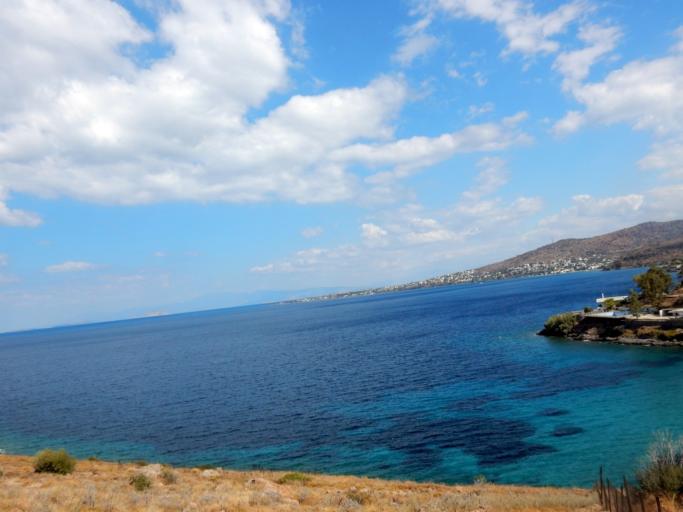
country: GR
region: Attica
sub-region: Nomos Piraios
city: Aegina
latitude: 37.6937
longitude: 23.4640
